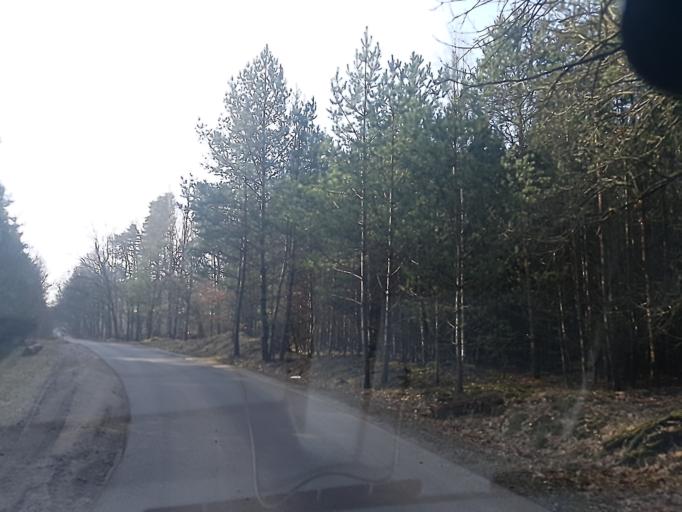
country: DE
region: Brandenburg
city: Wenzlow
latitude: 52.3520
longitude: 12.4648
